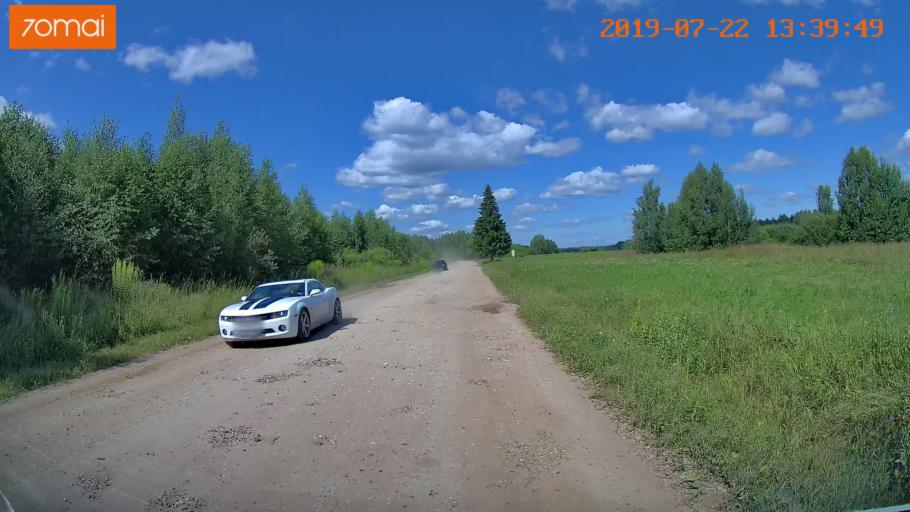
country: RU
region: Ivanovo
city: Novo-Talitsy
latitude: 57.0741
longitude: 40.8811
